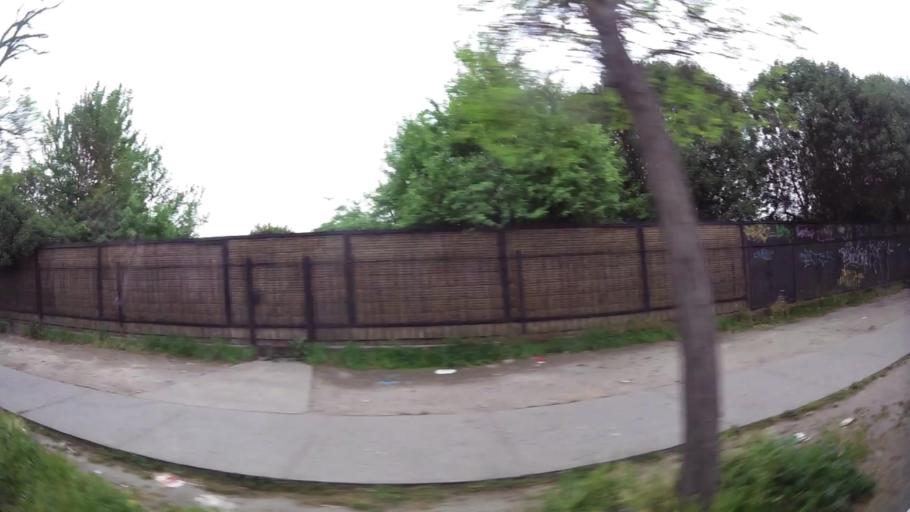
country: CL
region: Santiago Metropolitan
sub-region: Provincia de Santiago
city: Lo Prado
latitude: -33.5001
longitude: -70.7528
